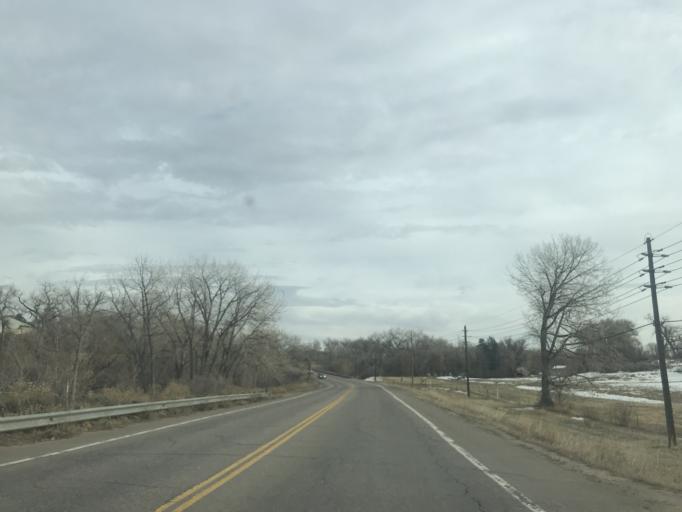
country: US
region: Colorado
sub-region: Douglas County
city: Highlands Ranch
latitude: 39.5644
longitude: -105.0039
